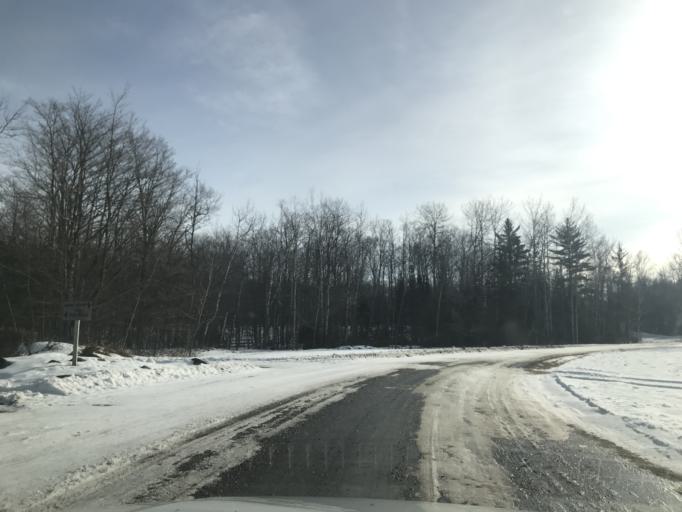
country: US
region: Wisconsin
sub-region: Door County
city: Sturgeon Bay
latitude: 45.1529
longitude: -87.0551
